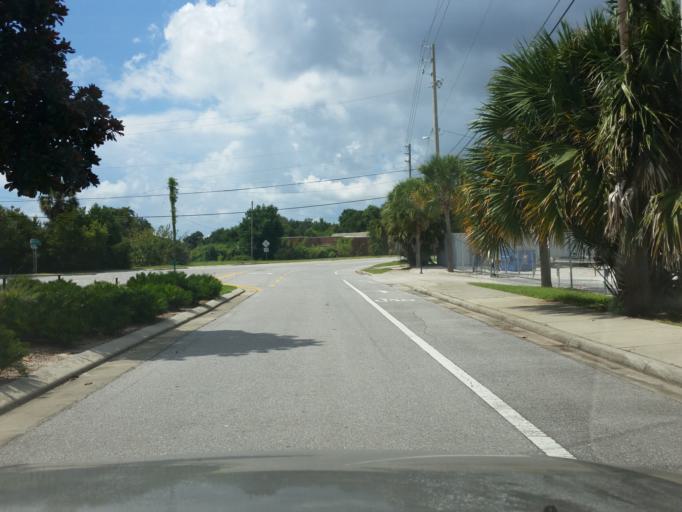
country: US
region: Florida
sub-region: Escambia County
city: Warrington
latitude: 30.3984
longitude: -87.2435
